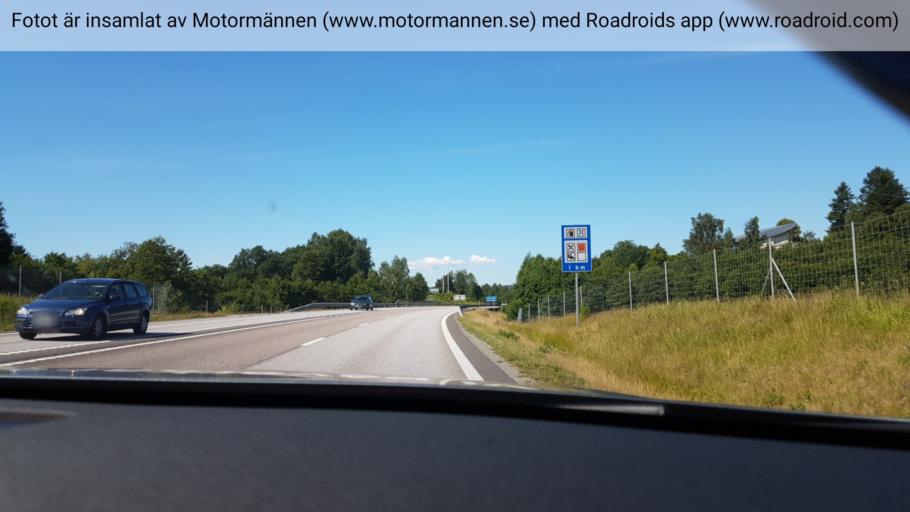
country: SE
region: Vaestra Goetaland
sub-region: Marks Kommun
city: Kinna
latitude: 57.5085
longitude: 12.7131
